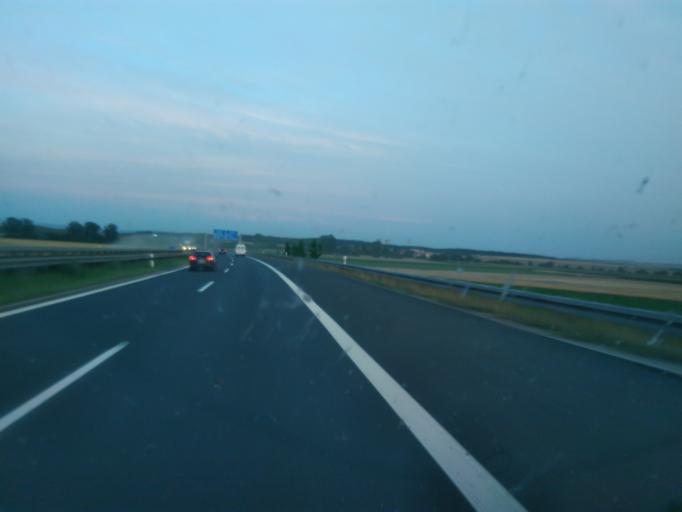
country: DE
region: Bavaria
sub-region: Regierungsbezirk Unterfranken
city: Geldersheim
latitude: 50.0300
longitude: 10.1413
